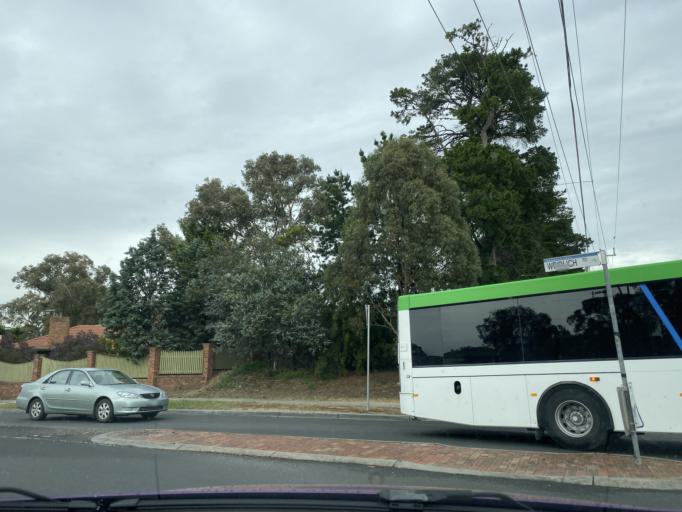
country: AU
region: Victoria
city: Saint Helena
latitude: -37.6876
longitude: 145.1348
